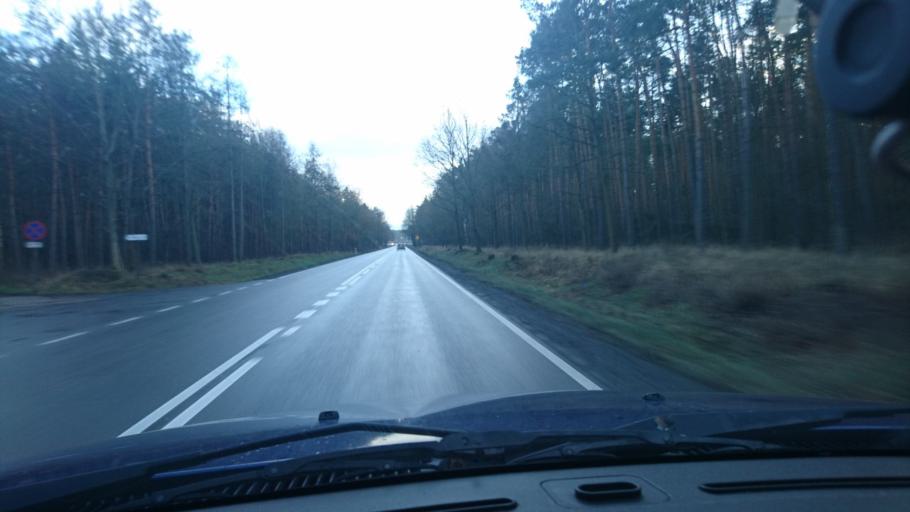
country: PL
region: Greater Poland Voivodeship
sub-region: Powiat kepinski
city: Kepno
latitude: 51.3366
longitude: 17.9543
